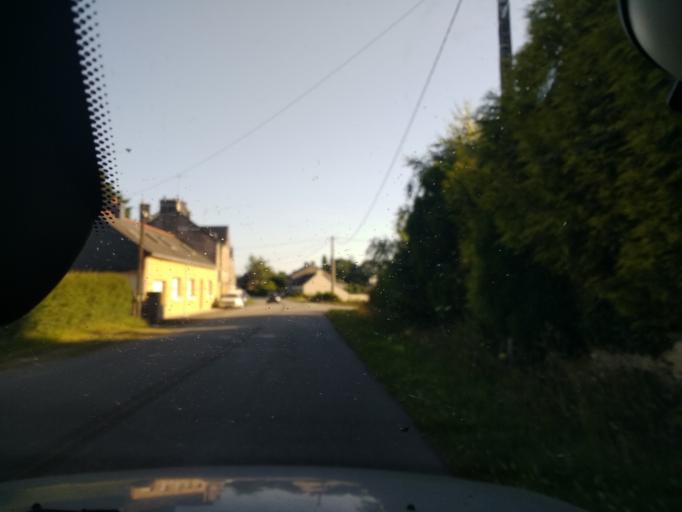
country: FR
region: Brittany
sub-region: Departement du Morbihan
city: Limerzel
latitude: 47.6430
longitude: -2.3599
